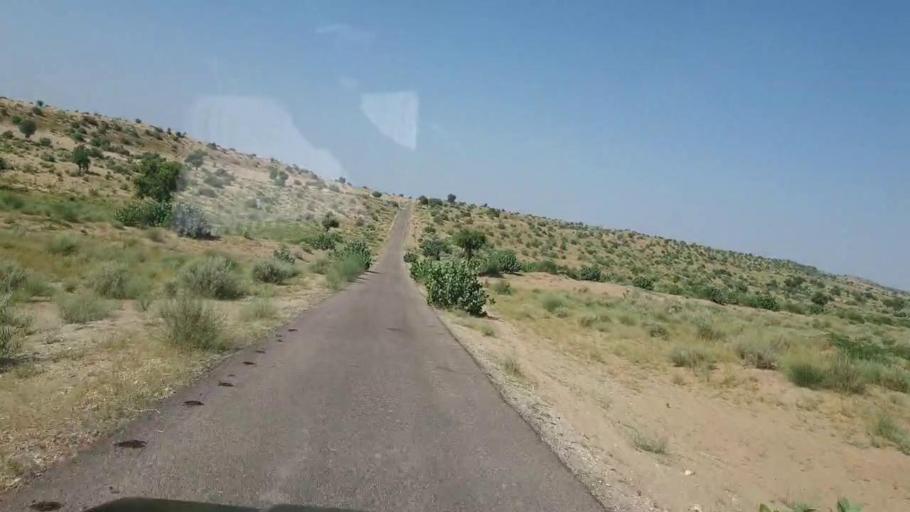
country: PK
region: Sindh
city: Chor
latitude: 25.6219
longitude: 70.3173
